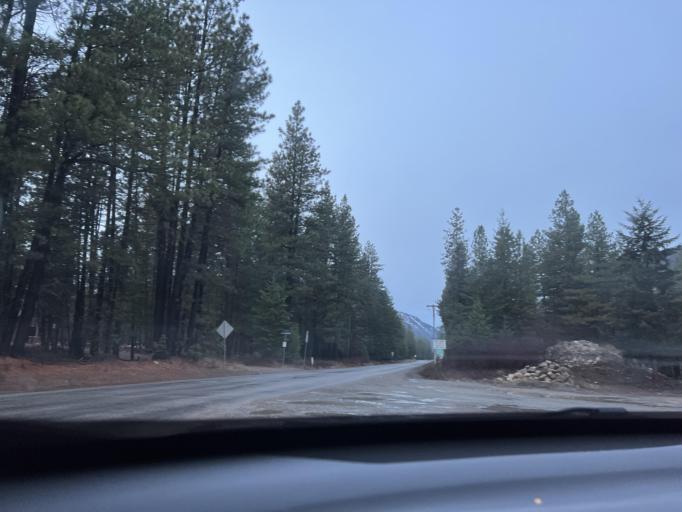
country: US
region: Washington
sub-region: Chelan County
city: Granite Falls
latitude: 48.5933
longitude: -120.4060
